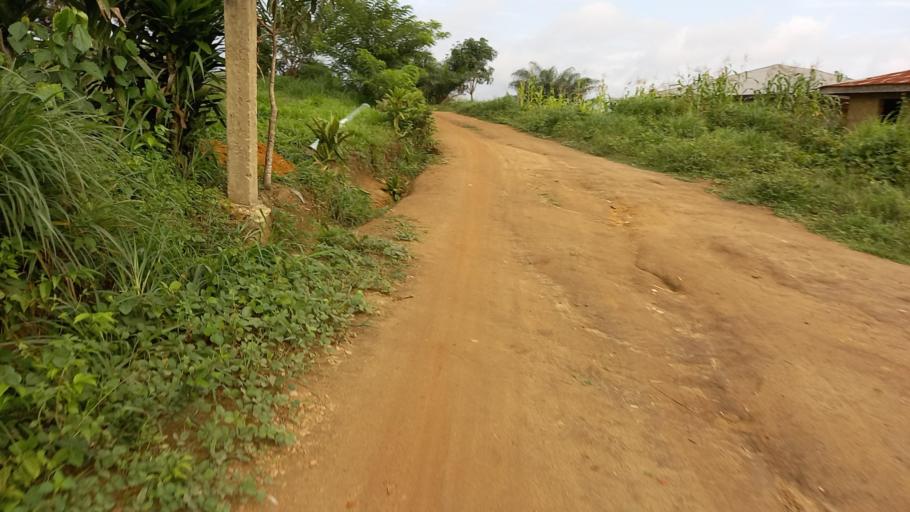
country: SL
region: Eastern Province
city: Kailahun
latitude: 8.2729
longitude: -10.5820
